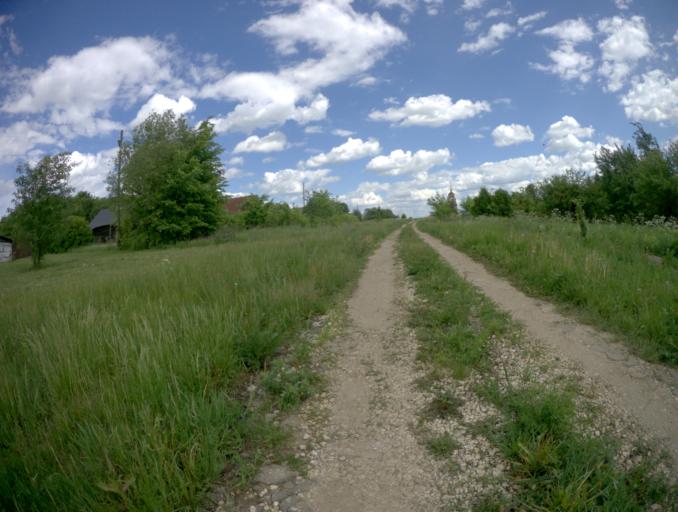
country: RU
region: Vladimir
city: Suzdal'
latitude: 56.4407
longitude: 40.3824
